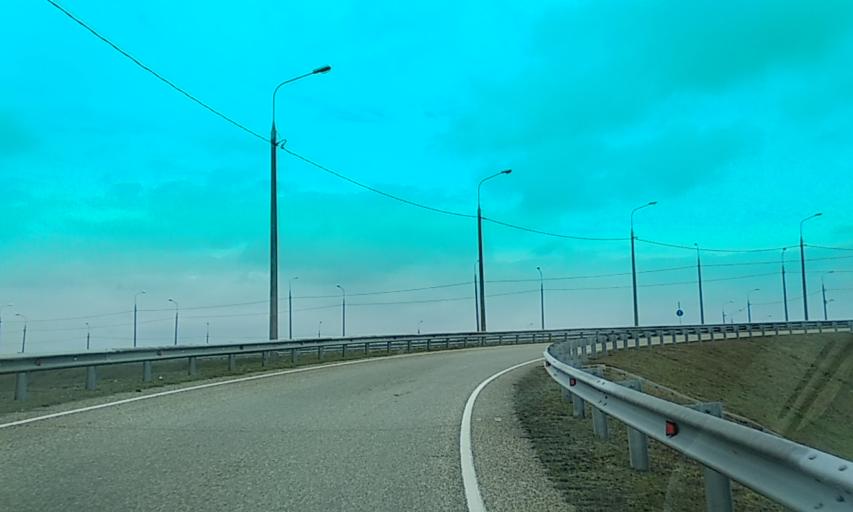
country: RU
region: Krasnodarskiy
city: Vyselki
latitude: 45.6157
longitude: 39.6950
